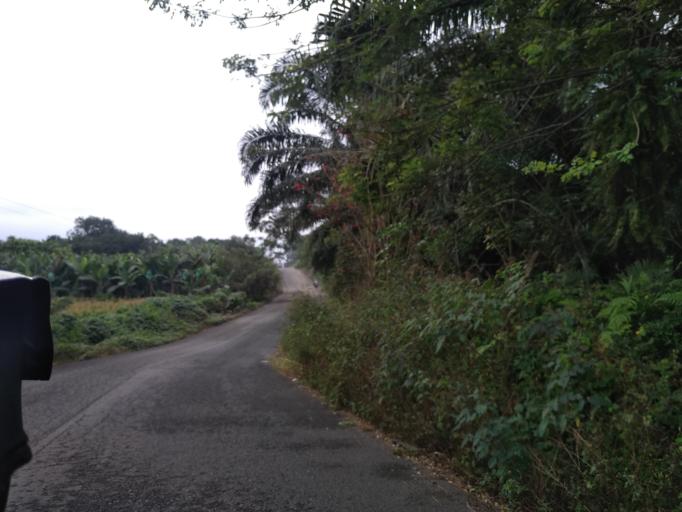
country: EC
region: Cotopaxi
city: La Mana
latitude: -0.9614
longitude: -79.3512
